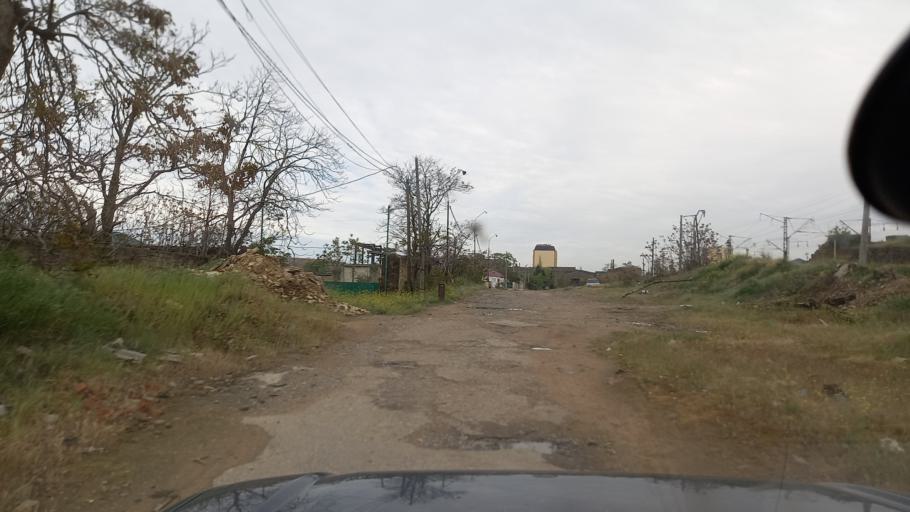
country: RU
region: Dagestan
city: Derbent
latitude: 42.0641
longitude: 48.3044
